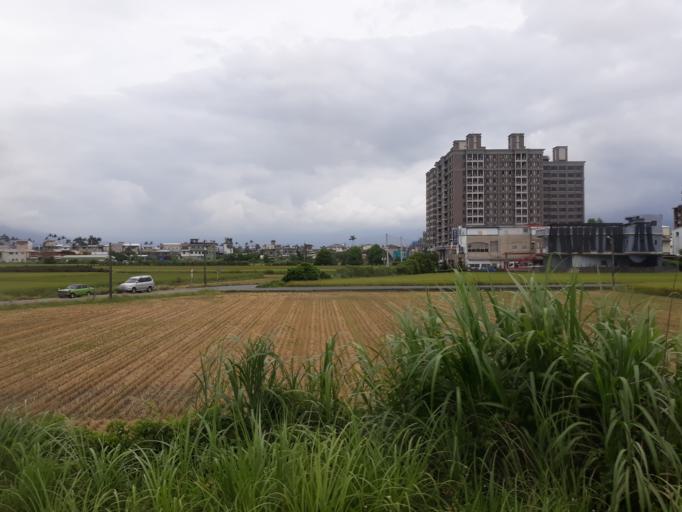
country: TW
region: Taiwan
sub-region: Yilan
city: Yilan
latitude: 24.6897
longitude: 121.7750
